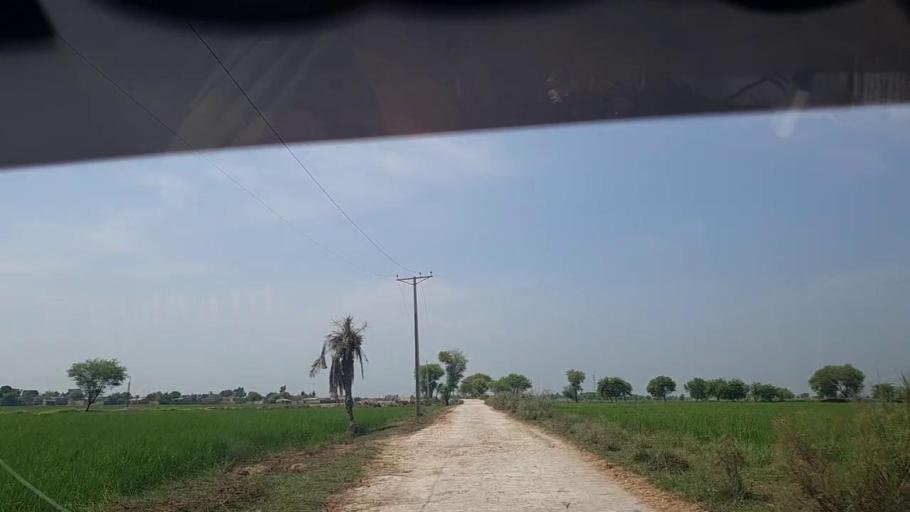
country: PK
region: Sindh
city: Thul
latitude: 28.1738
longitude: 68.7442
